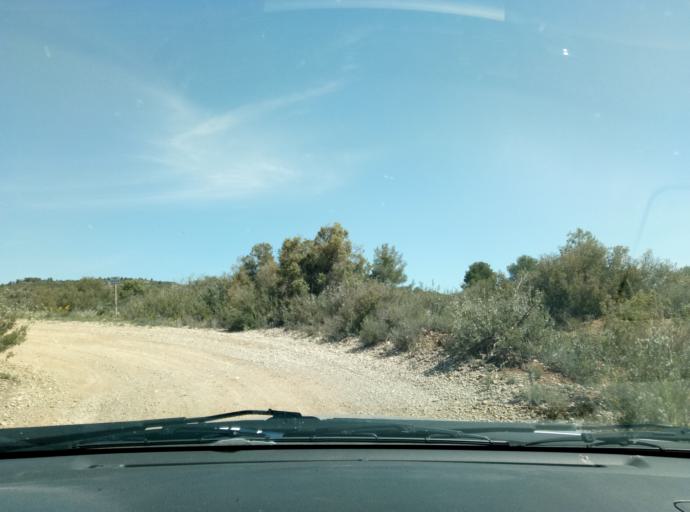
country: ES
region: Catalonia
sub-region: Provincia de Lleida
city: Juncosa
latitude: 41.4481
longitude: 0.7994
